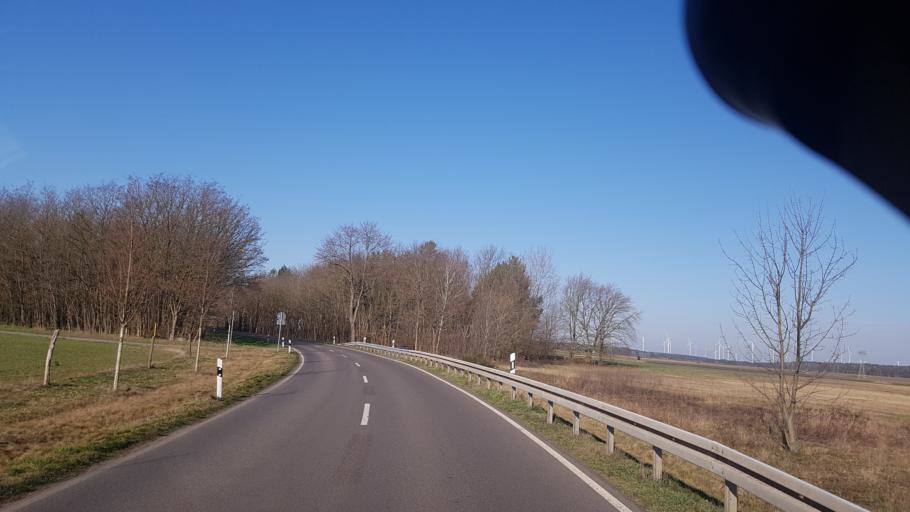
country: DE
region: Brandenburg
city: Luckau
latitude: 51.8490
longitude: 13.8177
